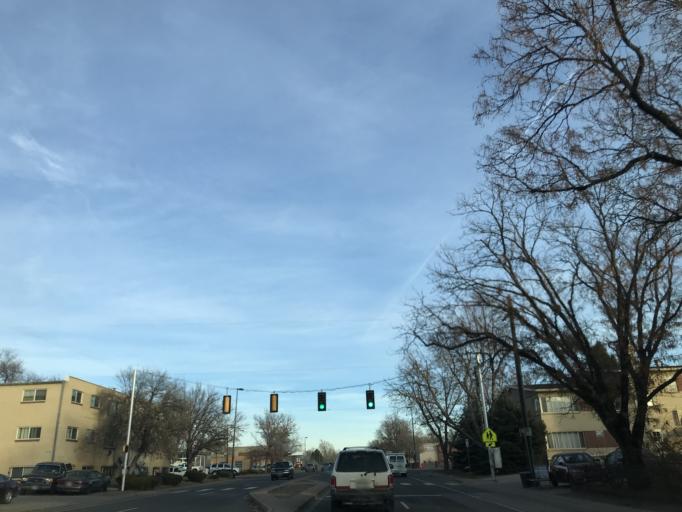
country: US
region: Colorado
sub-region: Adams County
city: Aurora
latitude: 39.7474
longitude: -104.8716
